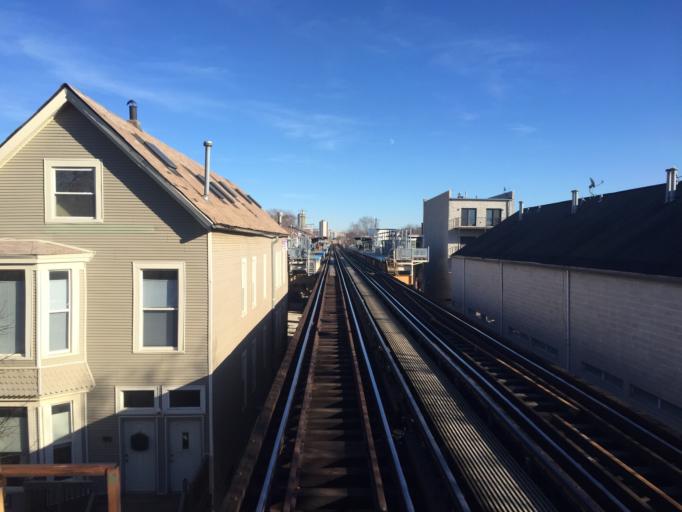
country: US
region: Illinois
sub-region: Cook County
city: Lincolnwood
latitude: 41.9438
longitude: -87.6648
